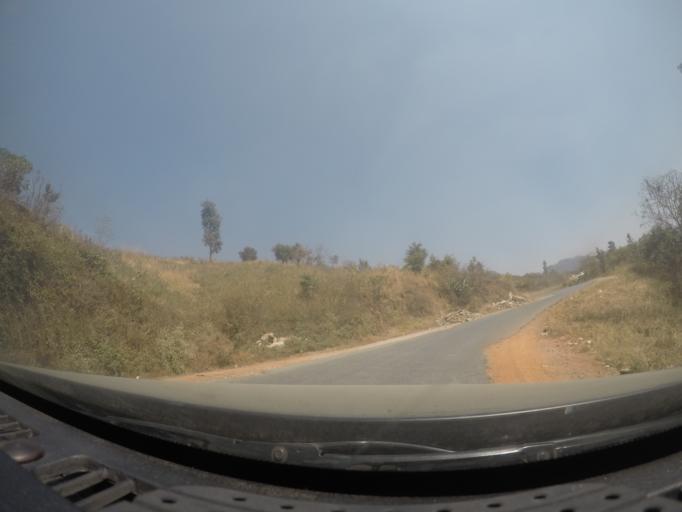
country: MM
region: Shan
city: Taunggyi
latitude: 20.8040
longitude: 97.2586
